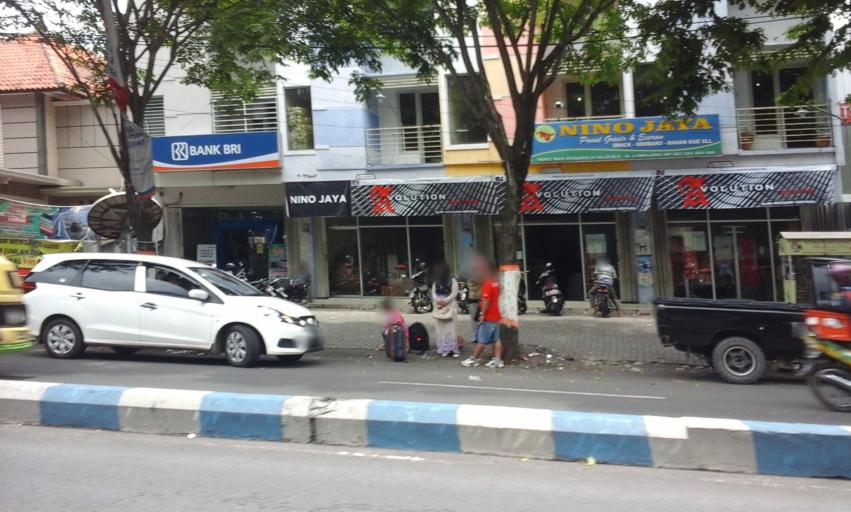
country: ID
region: East Java
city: Krajan
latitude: -8.0761
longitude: 113.2370
